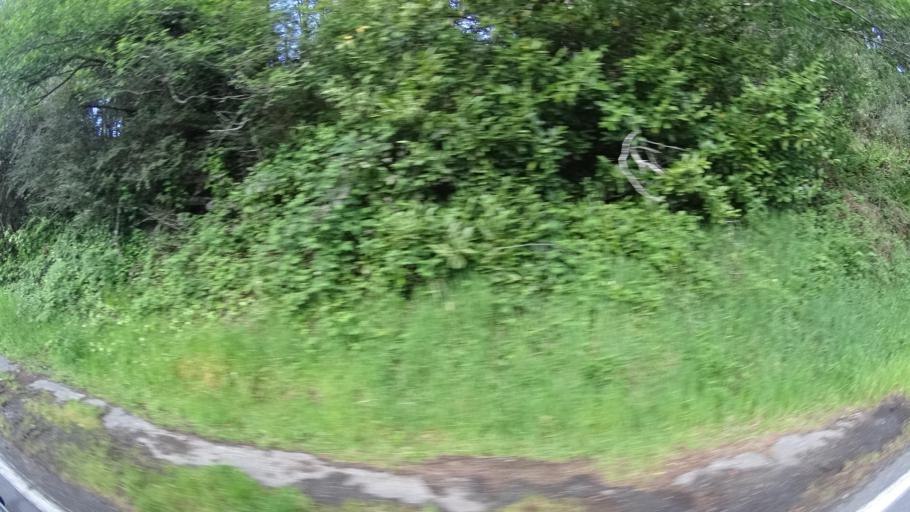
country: US
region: California
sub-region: Humboldt County
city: McKinleyville
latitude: 40.9892
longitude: -124.1103
